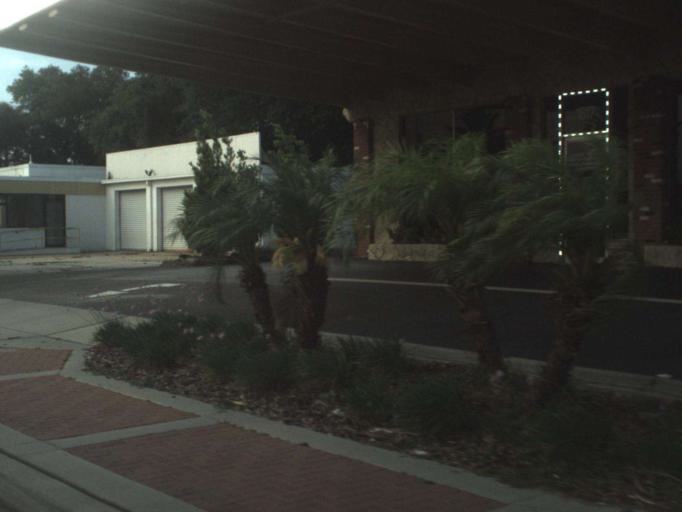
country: US
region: Florida
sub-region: Volusia County
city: South Daytona
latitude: 29.1826
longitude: -81.0078
